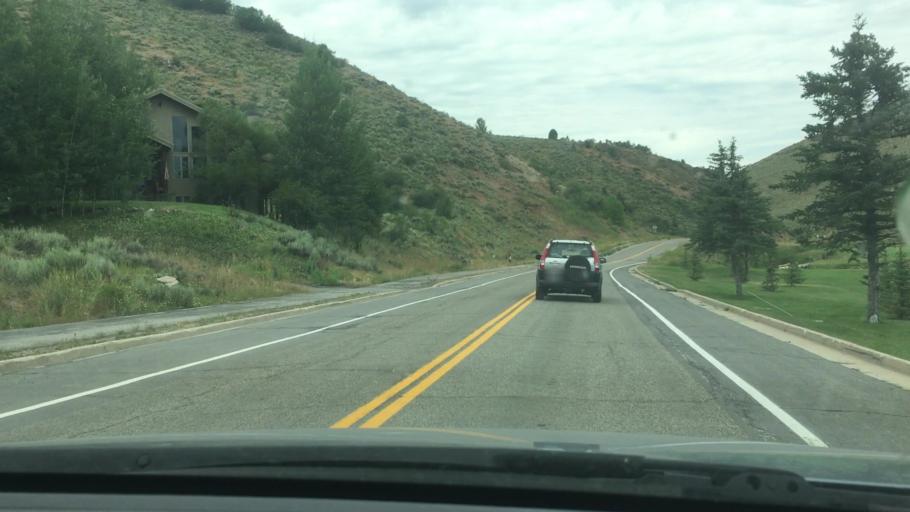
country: US
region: Utah
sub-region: Summit County
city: Summit Park
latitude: 40.7658
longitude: -111.5829
